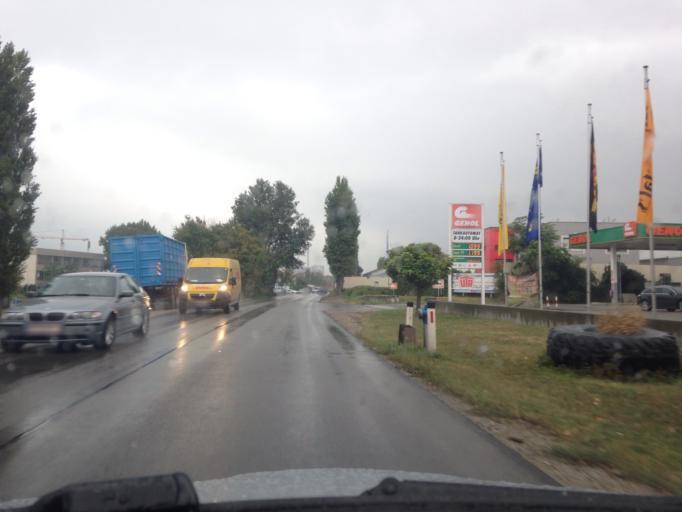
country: AT
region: Lower Austria
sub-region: Politischer Bezirk Wien-Umgebung
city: Schwechat
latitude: 48.1711
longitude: 16.4747
